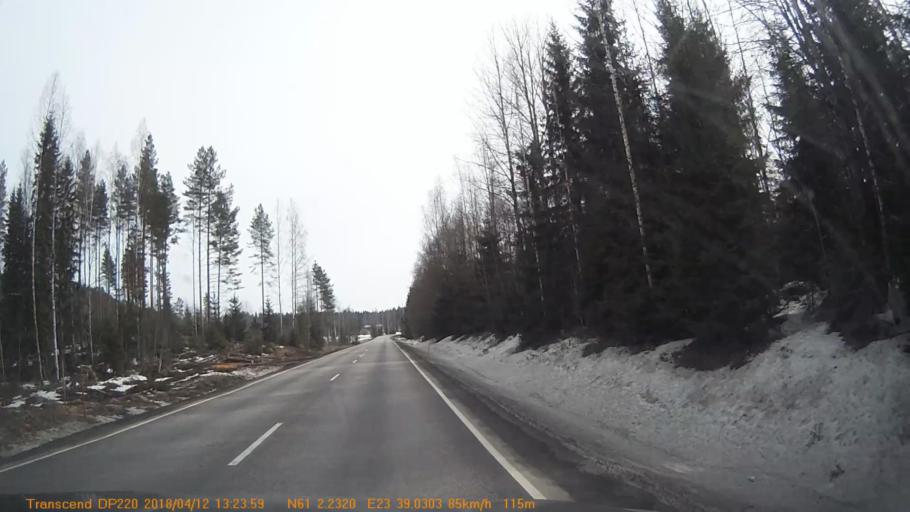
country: FI
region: Pirkanmaa
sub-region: Etelae-Pirkanmaa
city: Kylmaekoski
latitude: 61.0362
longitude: 23.6522
